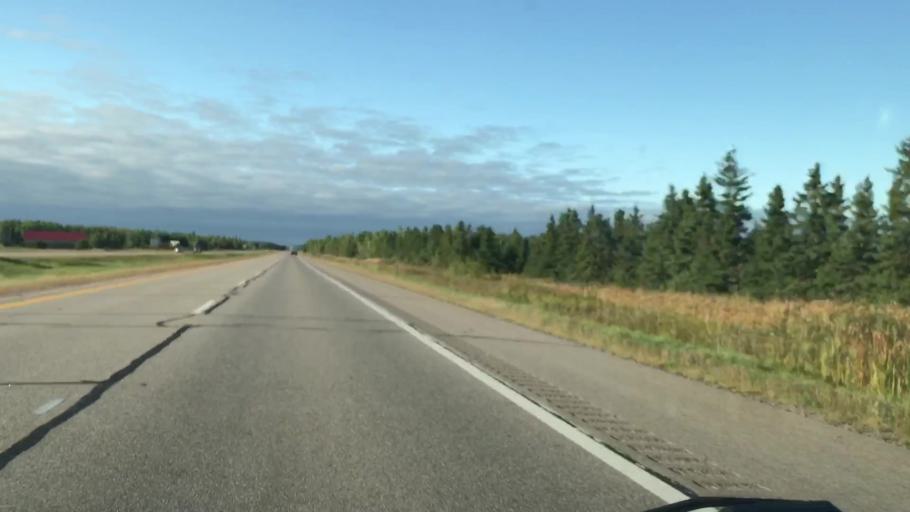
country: US
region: Michigan
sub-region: Chippewa County
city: Sault Ste. Marie
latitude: 46.4098
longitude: -84.3992
